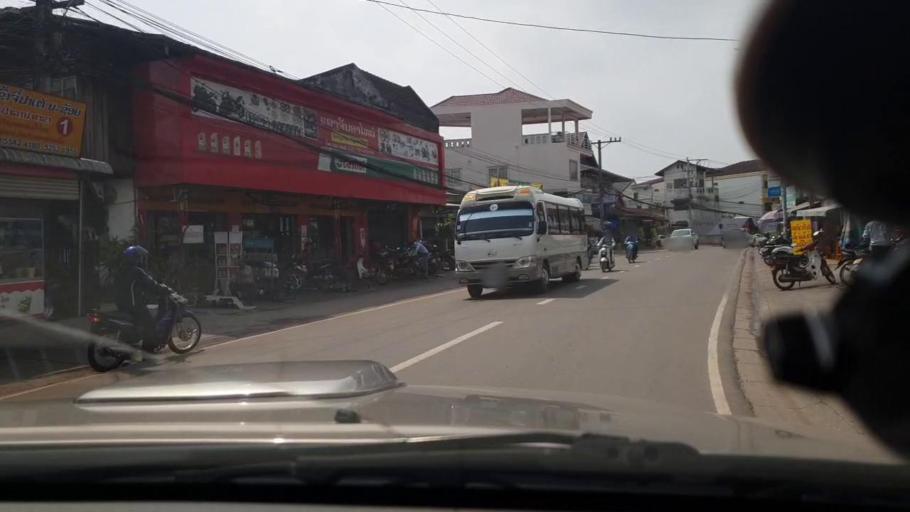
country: LA
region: Vientiane
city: Vientiane
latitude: 17.9578
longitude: 102.6237
